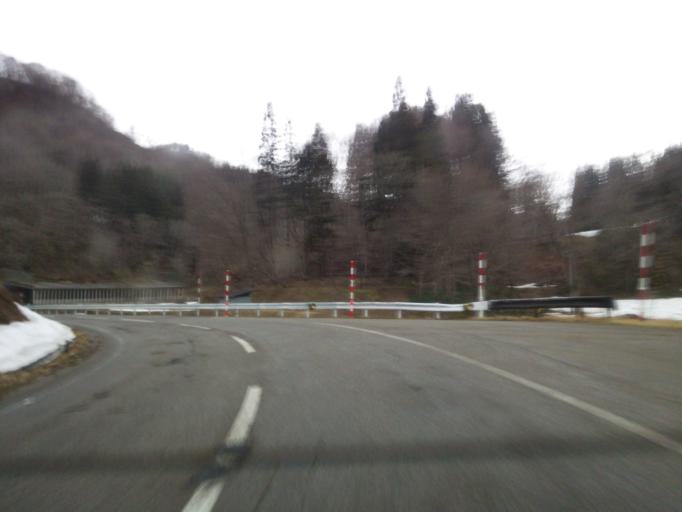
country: JP
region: Niigata
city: Muramatsu
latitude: 37.3346
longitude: 139.4706
